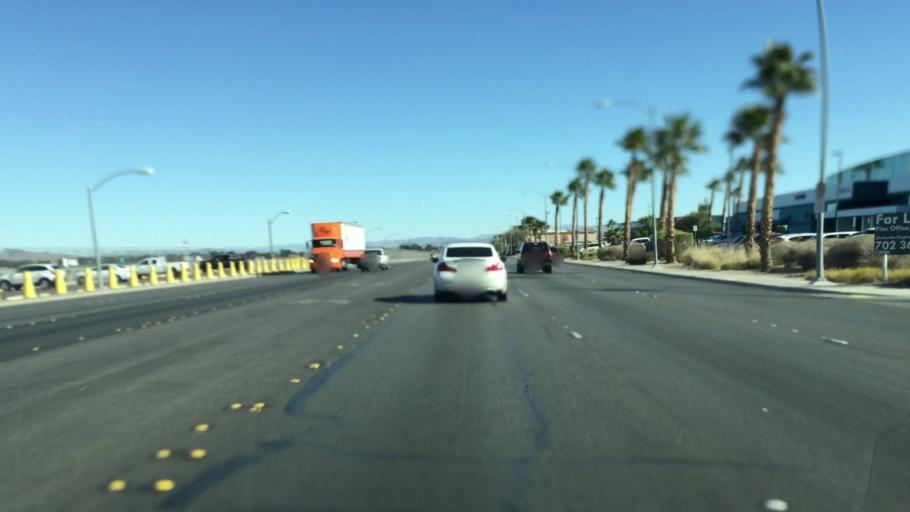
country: US
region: Nevada
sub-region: Clark County
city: Paradise
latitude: 36.0717
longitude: -115.1339
